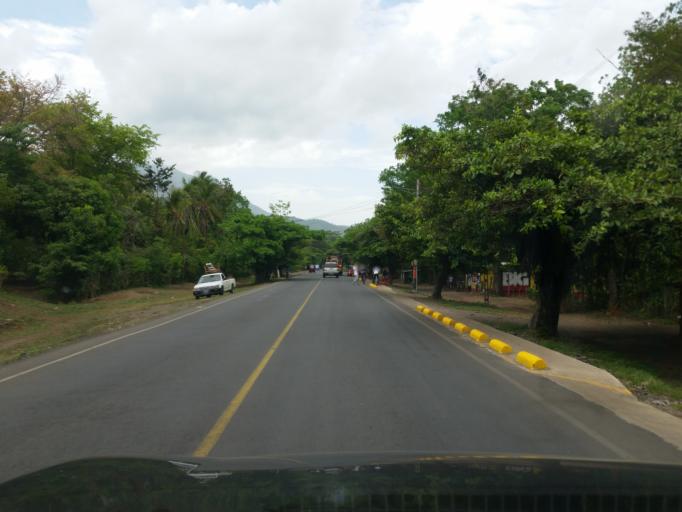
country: NI
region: Granada
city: Diriomo
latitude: 11.8698
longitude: -86.0377
